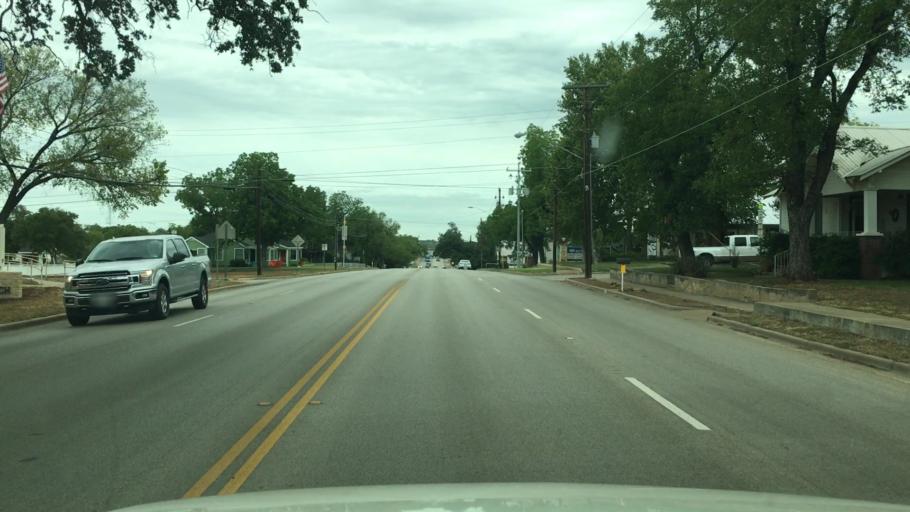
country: US
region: Texas
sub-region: Llano County
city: Llano
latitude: 30.7439
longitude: -98.6759
